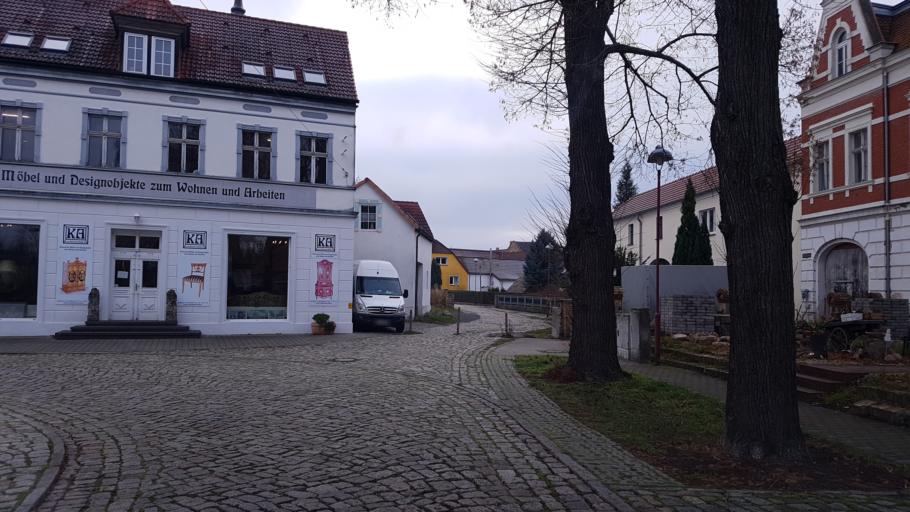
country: DE
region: Brandenburg
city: Schipkau
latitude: 51.5425
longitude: 13.8943
